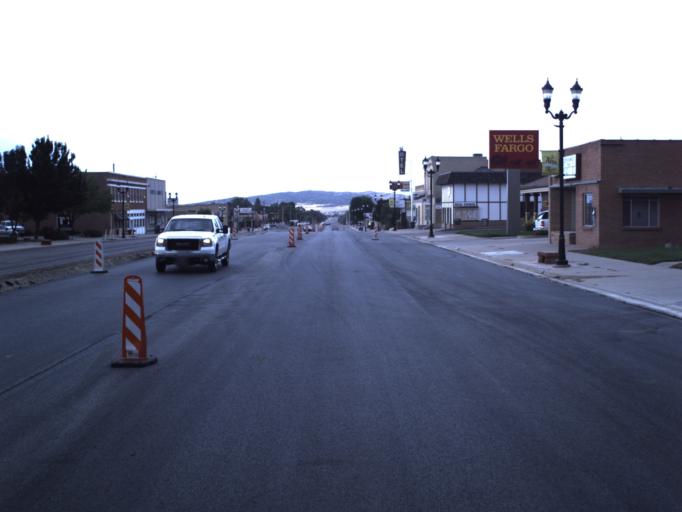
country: US
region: Utah
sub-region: Millard County
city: Fillmore
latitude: 38.9673
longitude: -112.3236
